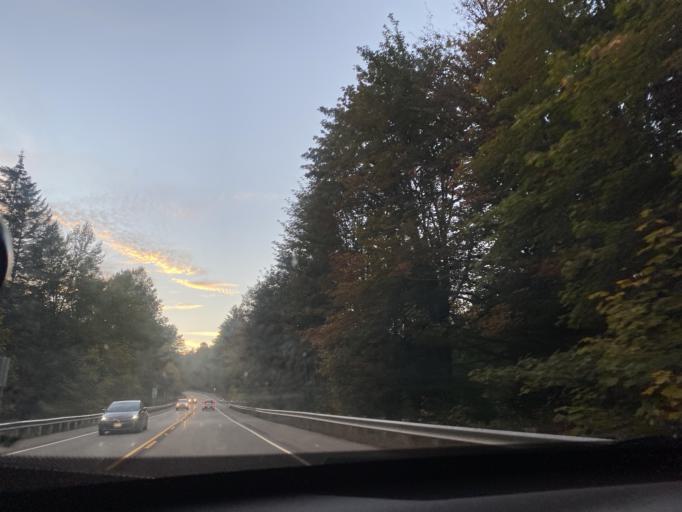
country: US
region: Washington
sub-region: Clallam County
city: Port Angeles
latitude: 48.0657
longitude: -123.5806
